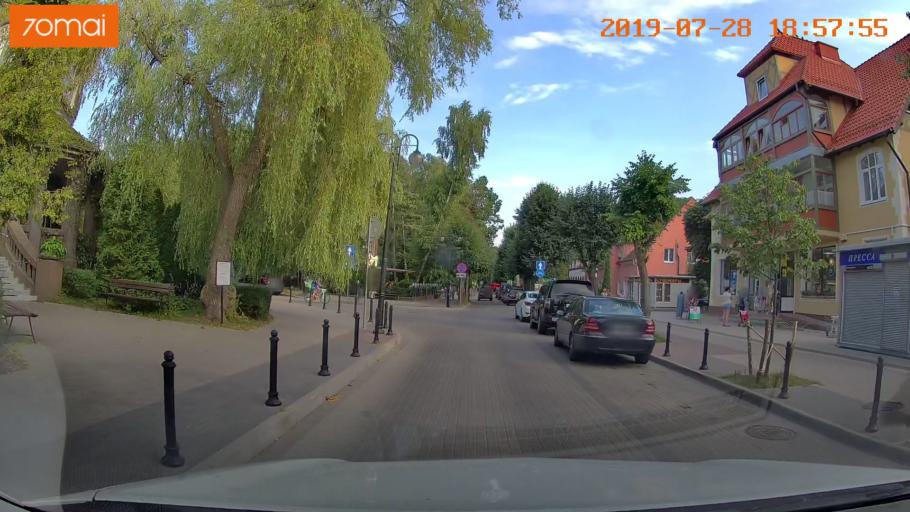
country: RU
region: Kaliningrad
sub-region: Gorod Svetlogorsk
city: Svetlogorsk
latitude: 54.9432
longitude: 20.1543
